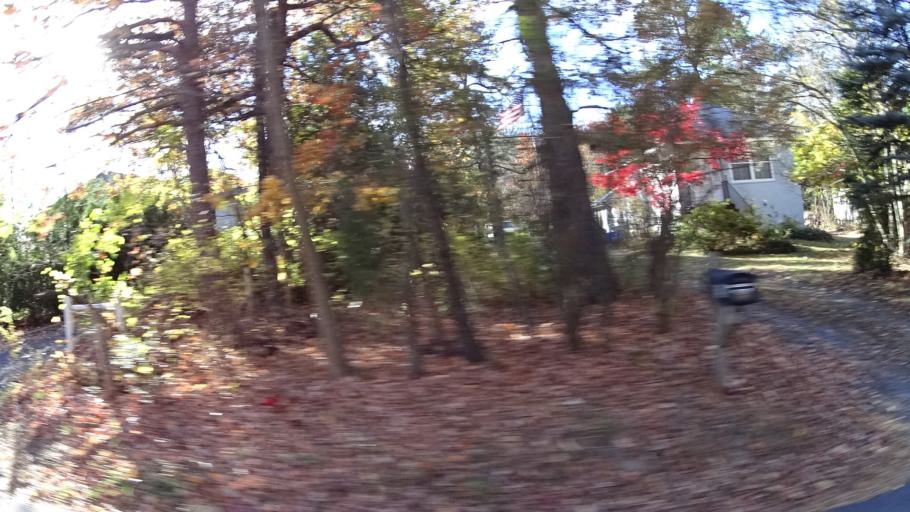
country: US
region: New Jersey
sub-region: Somerset County
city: Watchung
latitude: 40.6556
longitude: -74.4558
